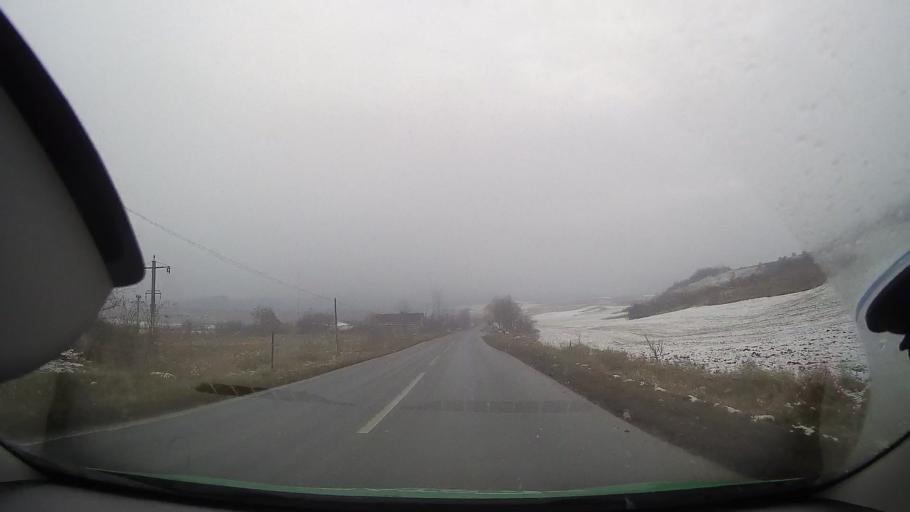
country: RO
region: Sibiu
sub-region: Comuna Blajel
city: Blajel
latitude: 46.2535
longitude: 24.2997
